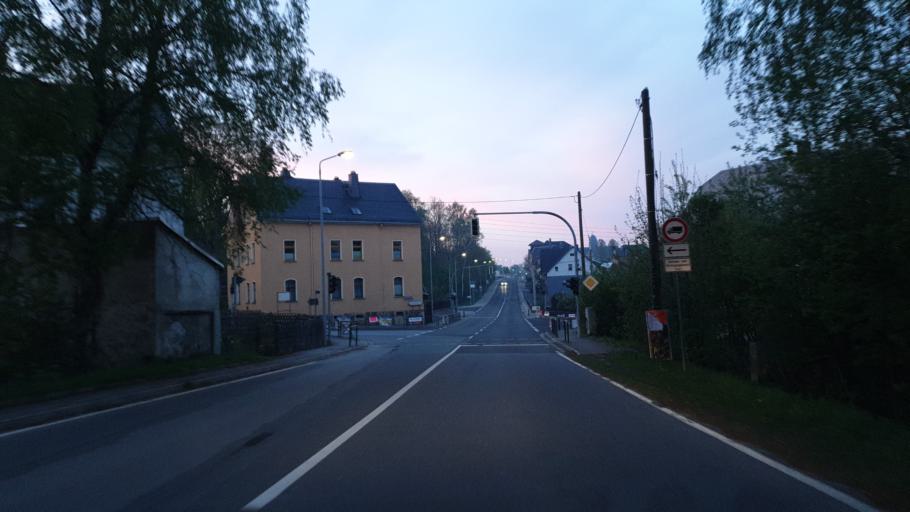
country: DE
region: Saxony
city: Stollberg
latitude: 50.7053
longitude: 12.7710
